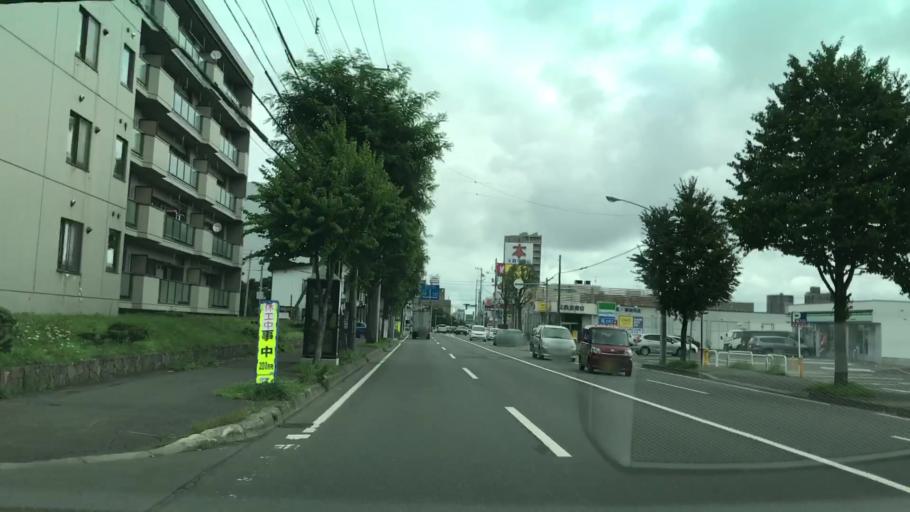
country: JP
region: Hokkaido
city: Sapporo
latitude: 43.0667
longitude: 141.3068
